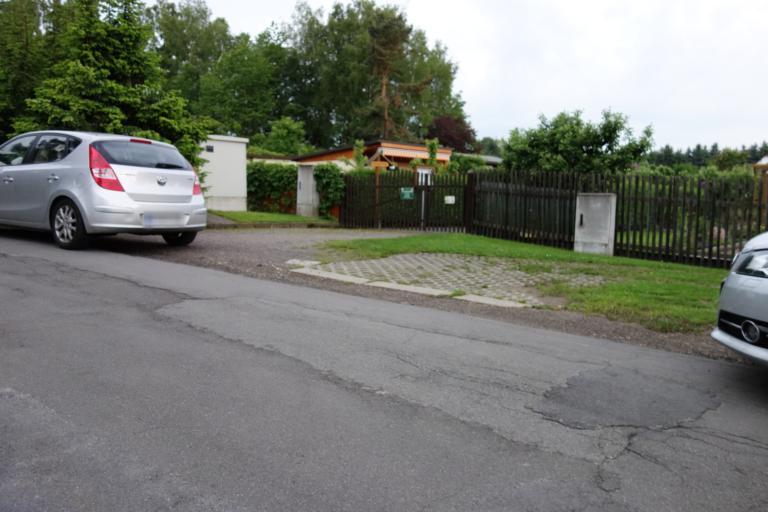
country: DE
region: Saxony
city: Freiberg
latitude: 50.8894
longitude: 13.3475
